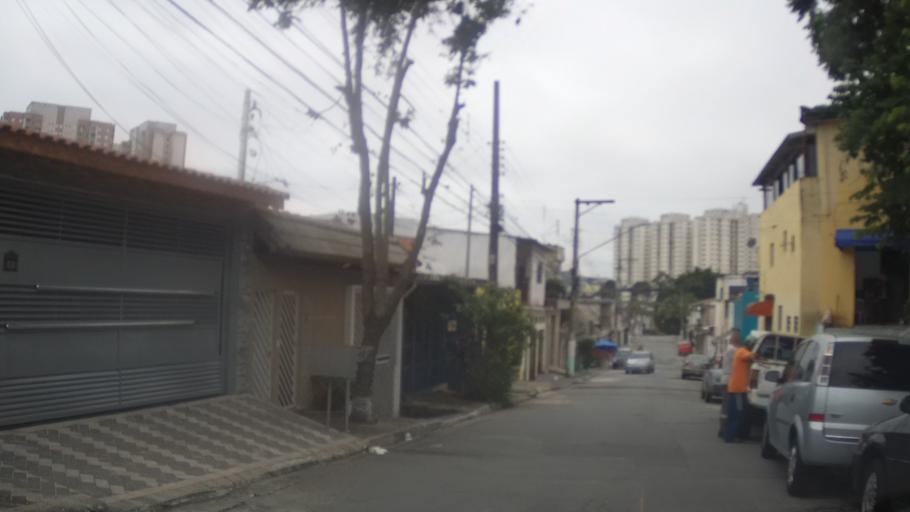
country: BR
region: Sao Paulo
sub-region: Guarulhos
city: Guarulhos
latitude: -23.4471
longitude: -46.5397
